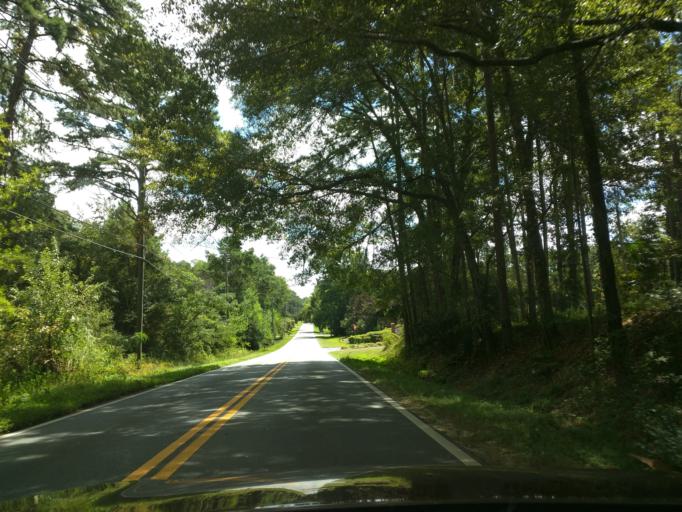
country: US
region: Florida
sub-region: Leon County
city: Tallahassee
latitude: 30.5874
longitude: -84.2640
